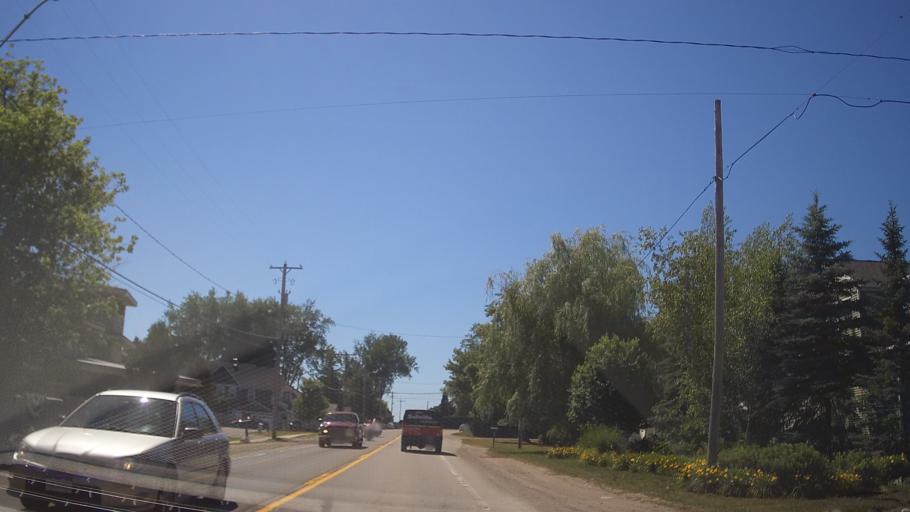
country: US
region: Michigan
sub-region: Emmet County
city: Petoskey
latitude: 45.4219
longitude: -84.8244
